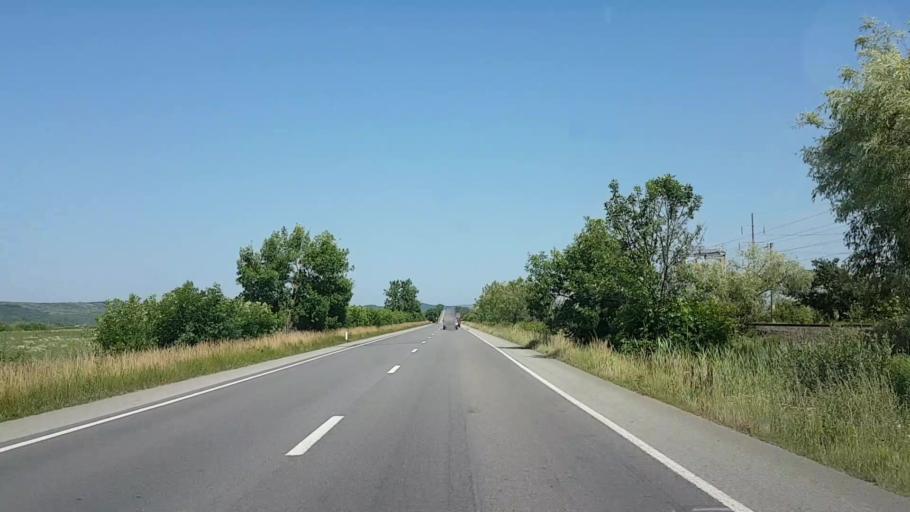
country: RO
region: Bistrita-Nasaud
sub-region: Comuna Sintereag
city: Cociu
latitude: 47.1833
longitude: 24.2227
